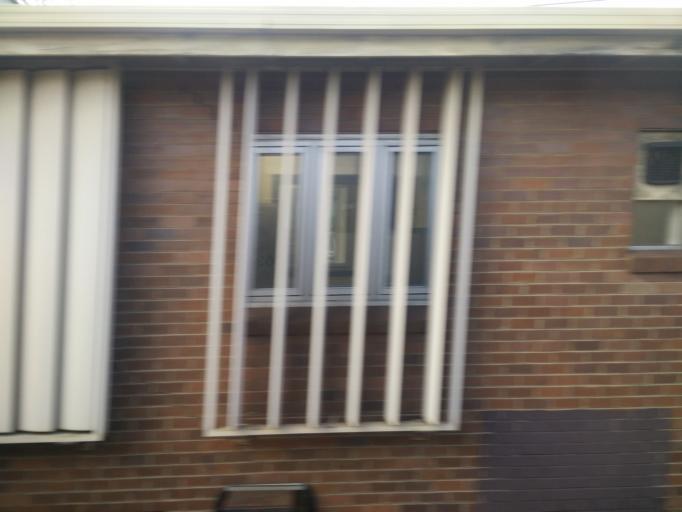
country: AU
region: New South Wales
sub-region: City of Sydney
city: Haymarket
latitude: -33.8849
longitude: 151.2063
